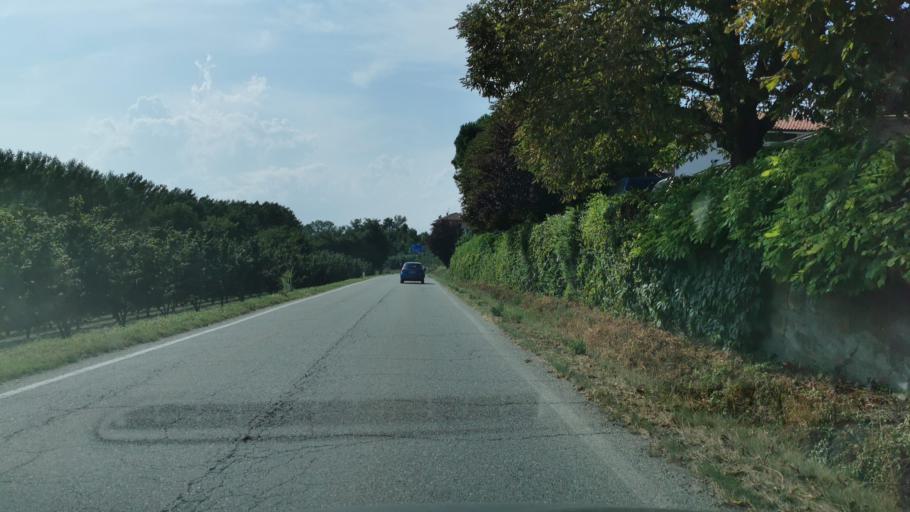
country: IT
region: Piedmont
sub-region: Provincia di Cuneo
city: Grinzane Cavour
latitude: 44.6522
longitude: 7.9884
